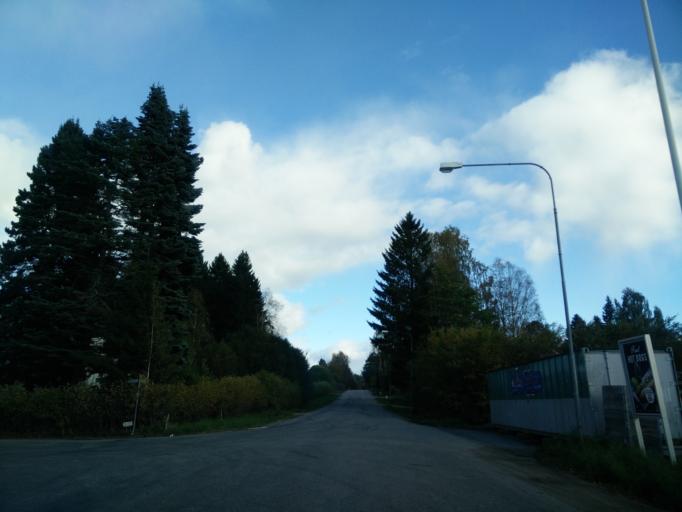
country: SE
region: Vaesternorrland
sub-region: Sundsvalls Kommun
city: Matfors
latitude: 62.3647
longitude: 17.0340
